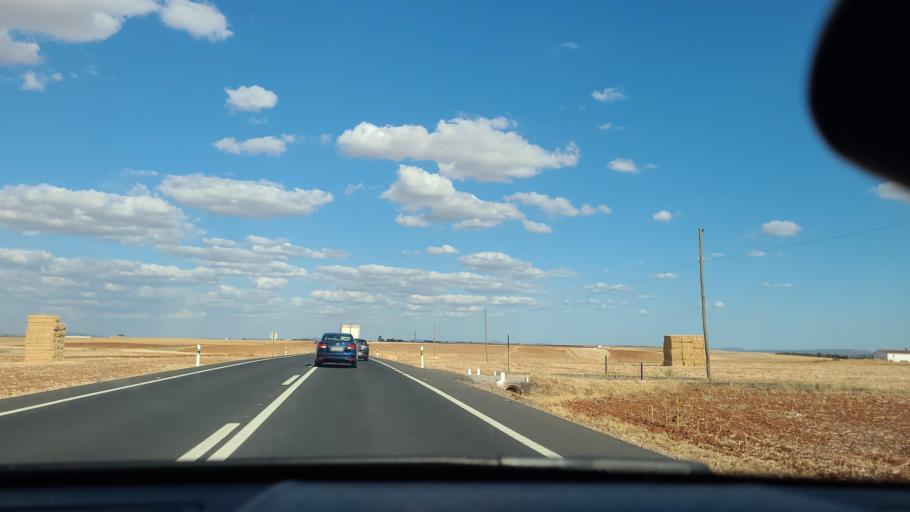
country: ES
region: Extremadura
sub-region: Provincia de Badajoz
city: Berlanga
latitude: 38.2652
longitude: -5.7549
